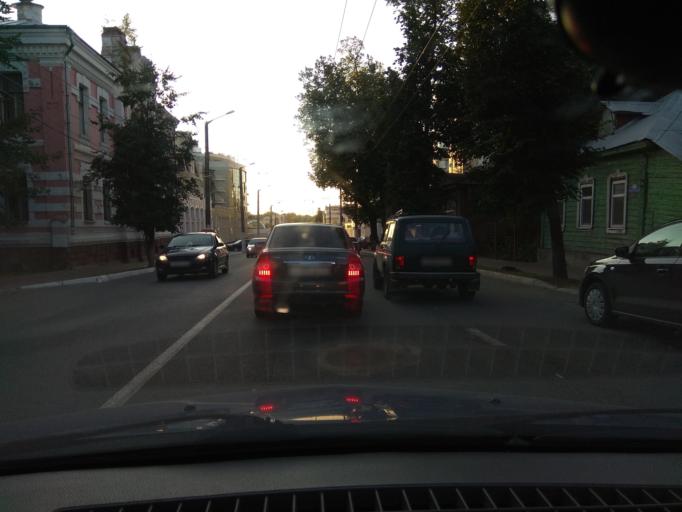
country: RU
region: Kaluga
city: Kaluga
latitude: 54.5124
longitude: 36.2422
